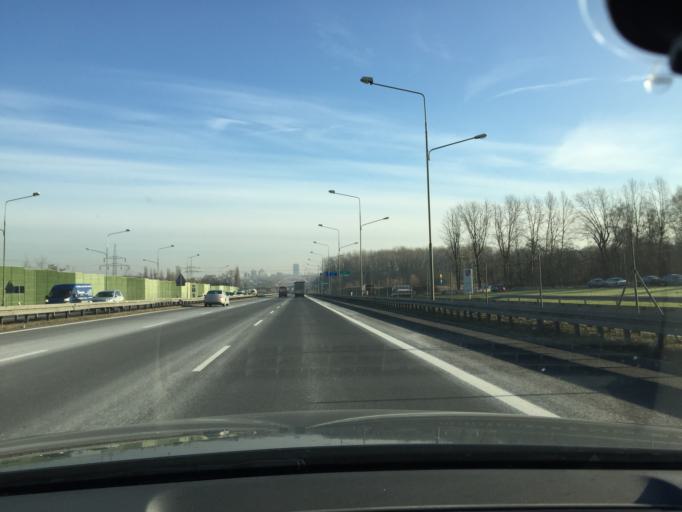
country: PL
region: Silesian Voivodeship
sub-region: Chorzow
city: Chorzow
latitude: 50.2551
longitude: 18.9716
